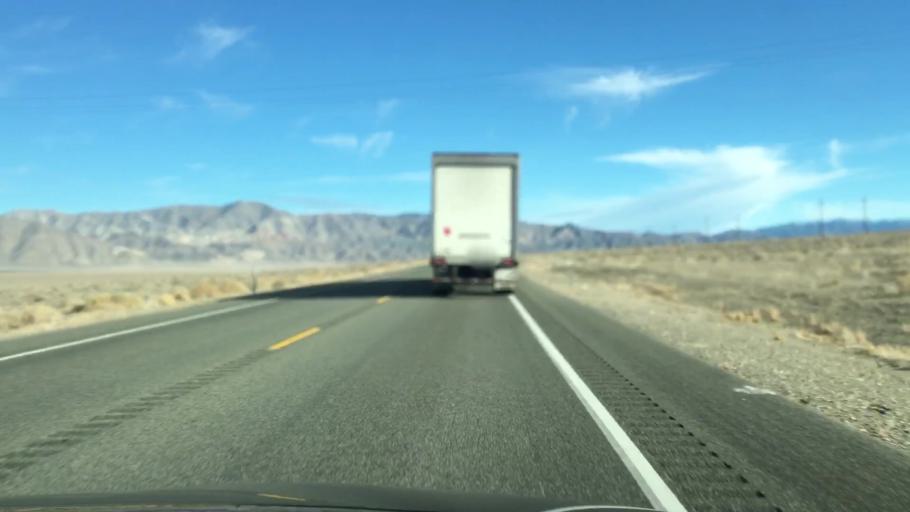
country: US
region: Nevada
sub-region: Mineral County
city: Hawthorne
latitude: 38.5280
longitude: -118.2411
